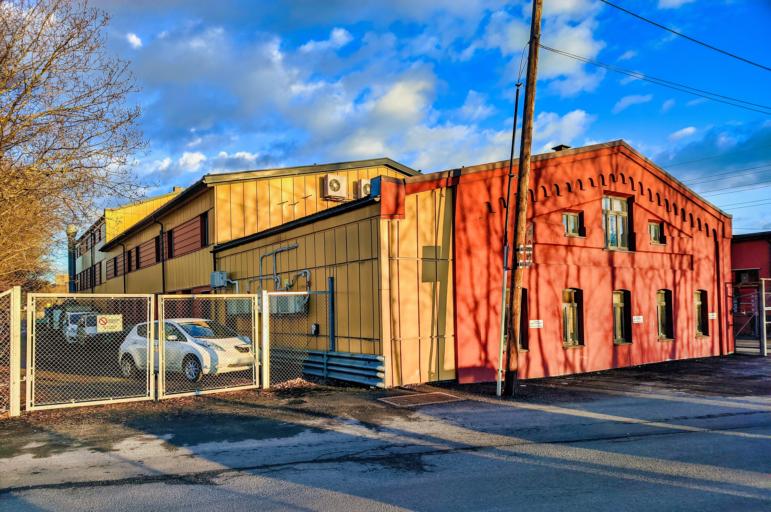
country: NO
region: Oslo
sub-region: Oslo
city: Oslo
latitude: 59.9263
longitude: 10.8350
